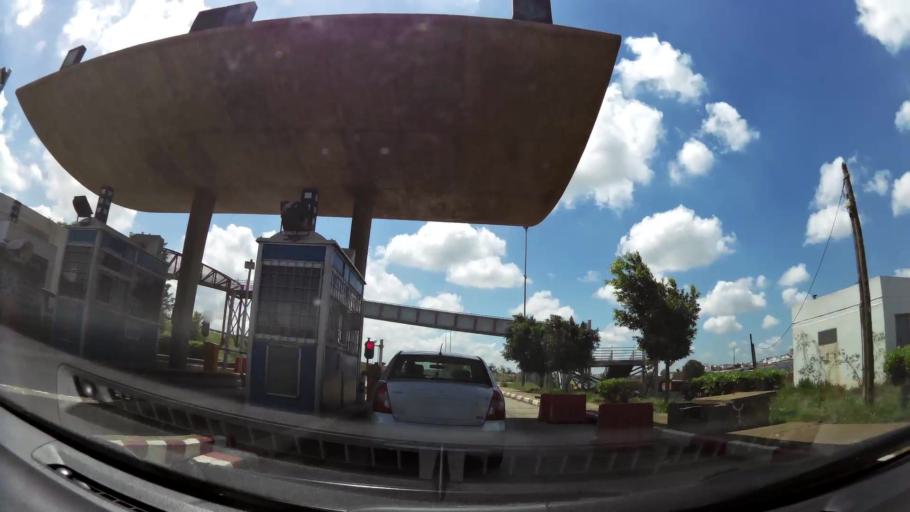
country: MA
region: Grand Casablanca
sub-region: Casablanca
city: Casablanca
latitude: 33.5271
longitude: -7.5691
